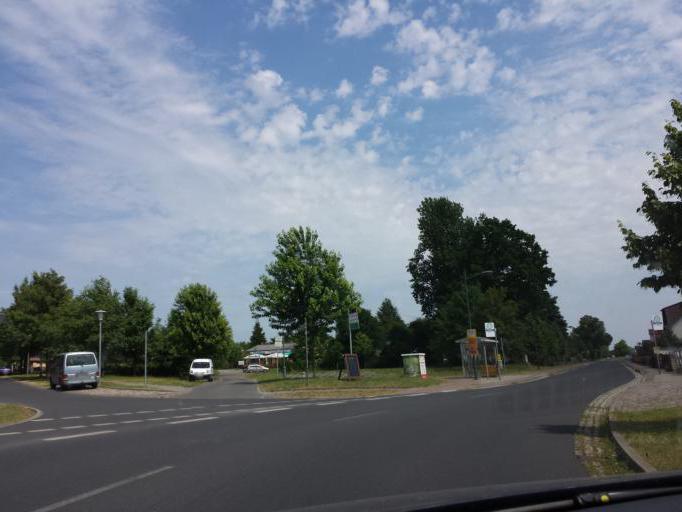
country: DE
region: Brandenburg
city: Kremmen
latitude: 52.8039
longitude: 13.0411
